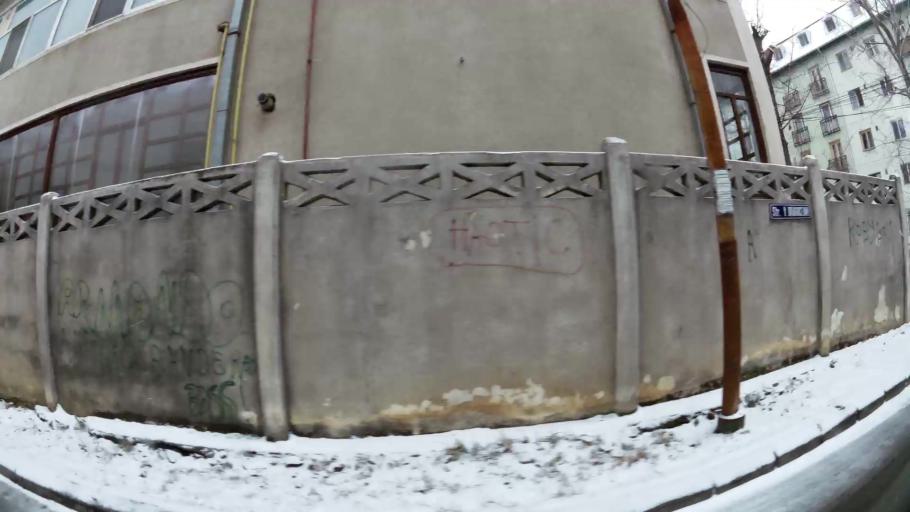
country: RO
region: Dambovita
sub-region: Municipiul Targoviste
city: Targoviste
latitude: 44.9217
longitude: 25.4687
